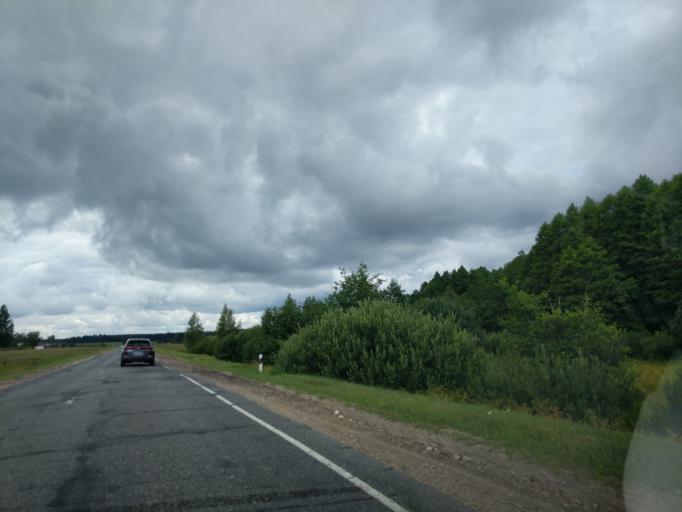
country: BY
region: Minsk
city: Il'ya
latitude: 54.4744
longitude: 27.2668
